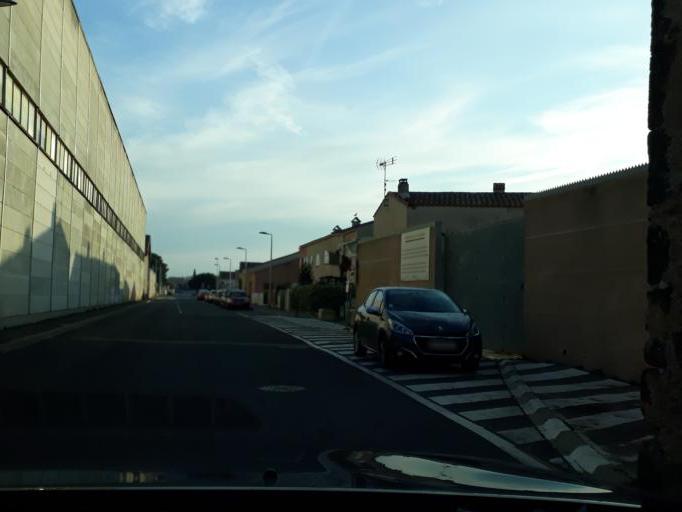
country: FR
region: Languedoc-Roussillon
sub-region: Departement de l'Herault
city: Marseillan
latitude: 43.3531
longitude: 3.5306
